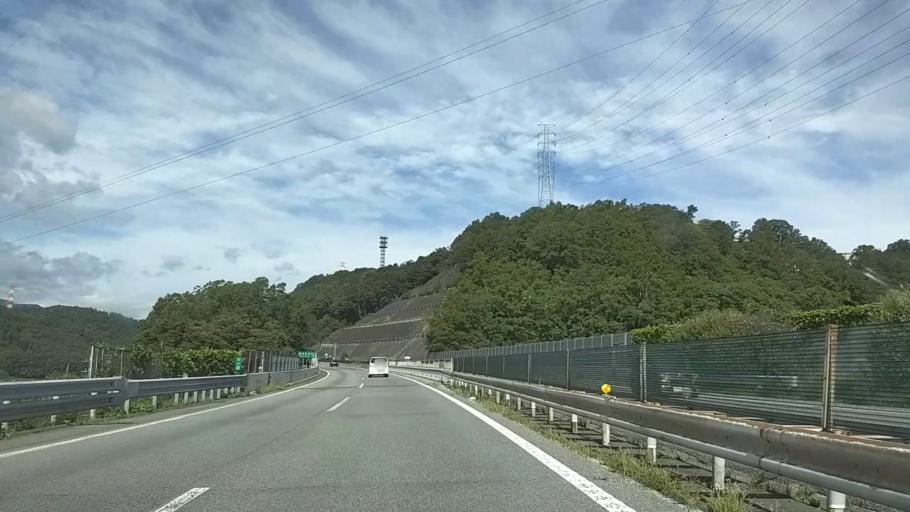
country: JP
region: Yamanashi
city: Nirasaki
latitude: 35.7843
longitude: 138.4189
